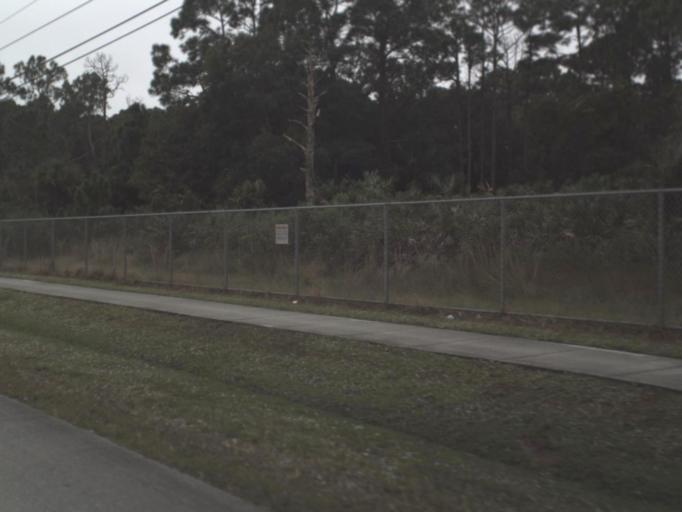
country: US
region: Florida
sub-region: Brevard County
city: June Park
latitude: 28.0246
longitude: -80.6719
